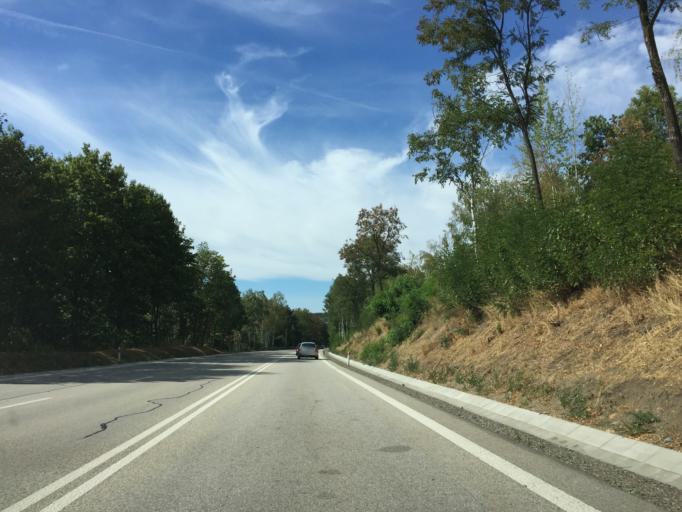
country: CZ
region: Central Bohemia
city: Votice
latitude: 49.6460
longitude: 14.6396
